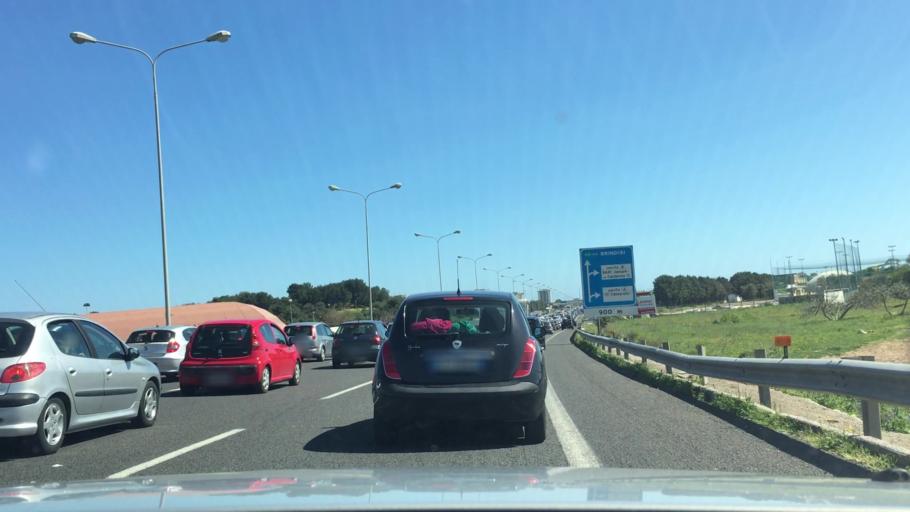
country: IT
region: Apulia
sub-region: Provincia di Bari
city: Triggiano
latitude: 41.0972
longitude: 16.9015
